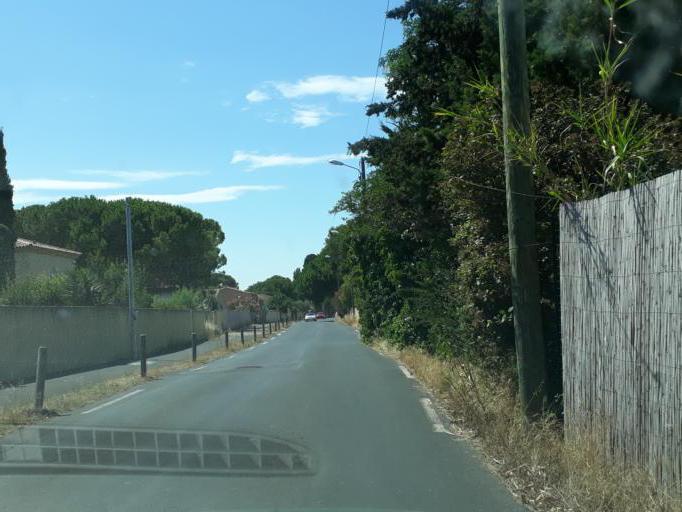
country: FR
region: Languedoc-Roussillon
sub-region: Departement de l'Herault
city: Agde
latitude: 43.2918
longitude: 3.4599
